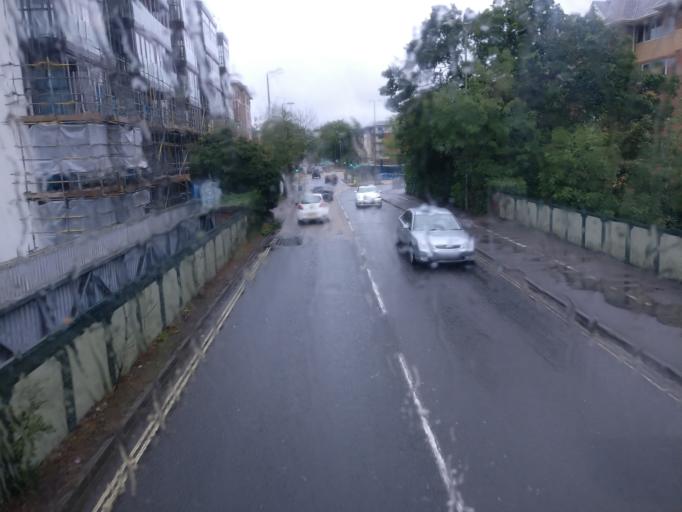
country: GB
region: England
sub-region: Hampshire
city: Farnborough
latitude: 51.2972
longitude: -0.7532
